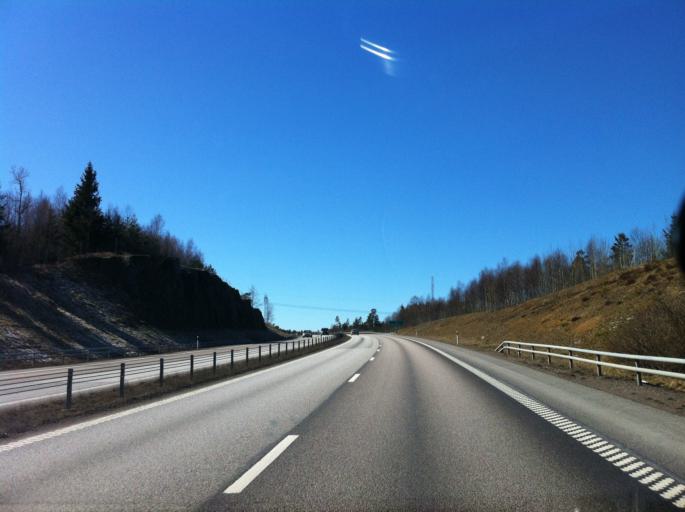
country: SE
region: Vaestra Goetaland
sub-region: Vanersborgs Kommun
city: Vanersborg
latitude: 58.3756
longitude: 12.3407
